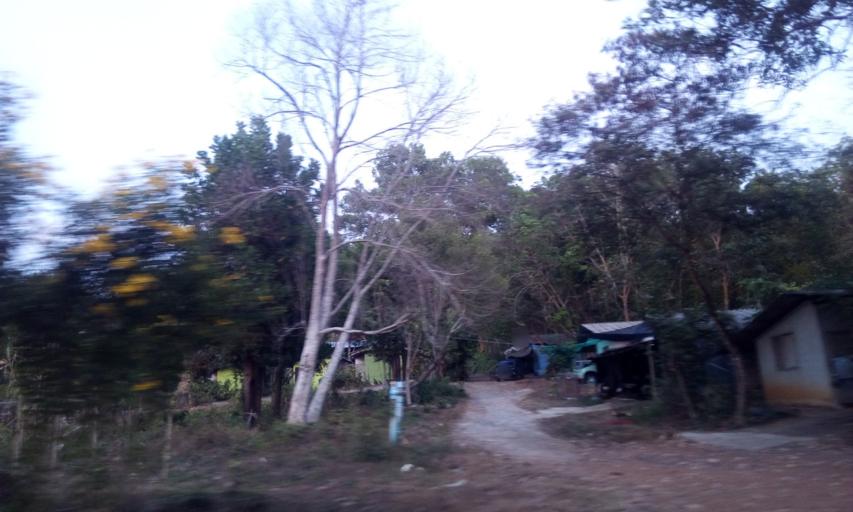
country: TH
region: Trat
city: Laem Ngop
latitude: 12.1959
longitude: 102.2883
